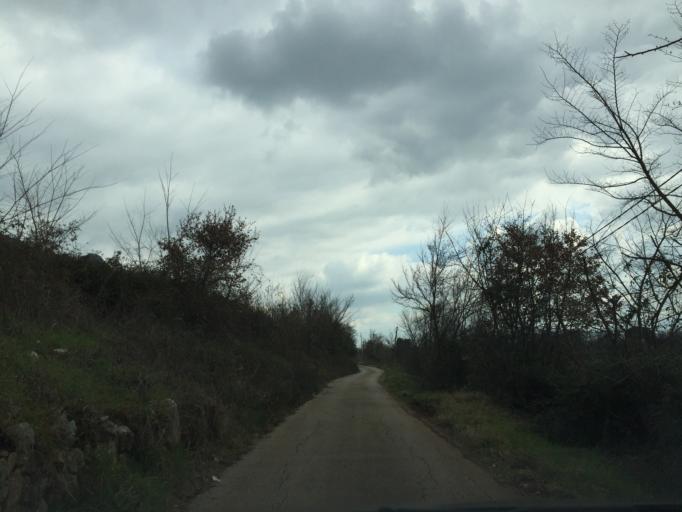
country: IT
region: Latium
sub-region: Provincia di Frosinone
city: Villa Santa Lucia
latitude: 41.4893
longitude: 13.7865
